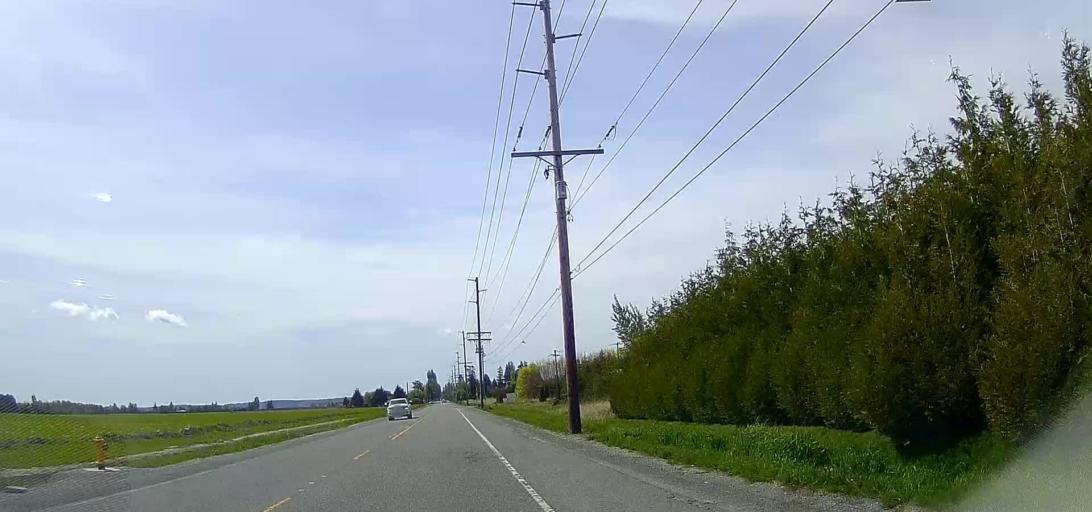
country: US
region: Washington
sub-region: Skagit County
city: Mount Vernon
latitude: 48.4209
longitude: -122.3765
